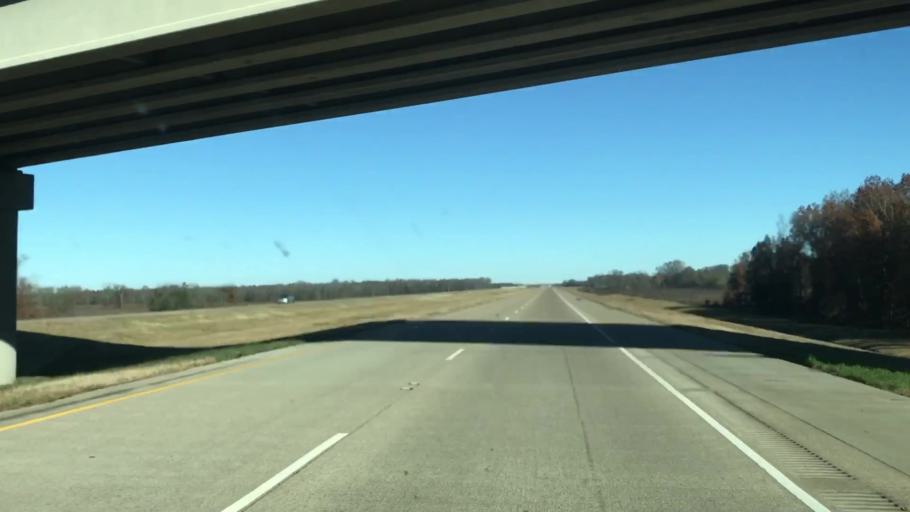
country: US
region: Louisiana
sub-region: Caddo Parish
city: Blanchard
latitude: 32.6163
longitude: -93.8350
